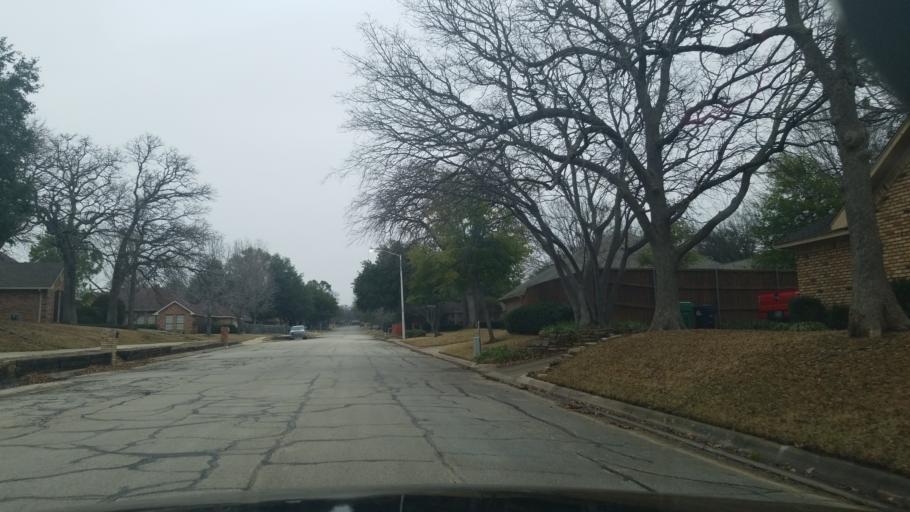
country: US
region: Texas
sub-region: Denton County
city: Denton
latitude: 33.1776
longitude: -97.1191
